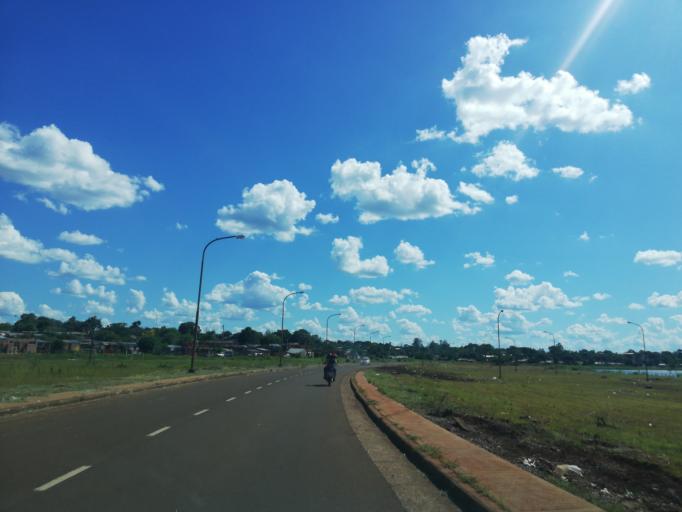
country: AR
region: Misiones
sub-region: Departamento de Capital
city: Posadas
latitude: -27.4185
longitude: -55.8872
